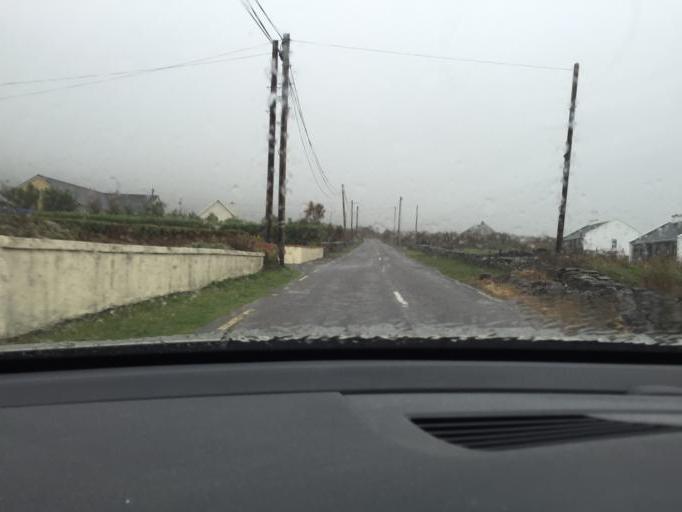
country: IE
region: Munster
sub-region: Ciarrai
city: Dingle
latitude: 52.1339
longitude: -10.4515
